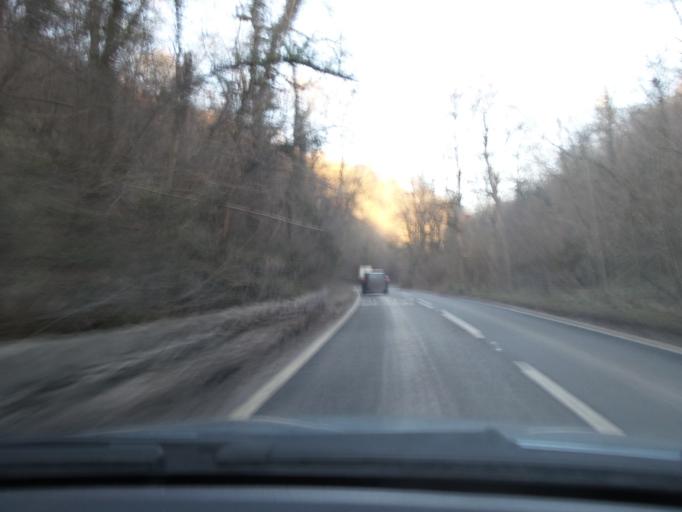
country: GB
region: England
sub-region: Derbyshire
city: Wirksworth
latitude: 53.1044
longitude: -1.6138
